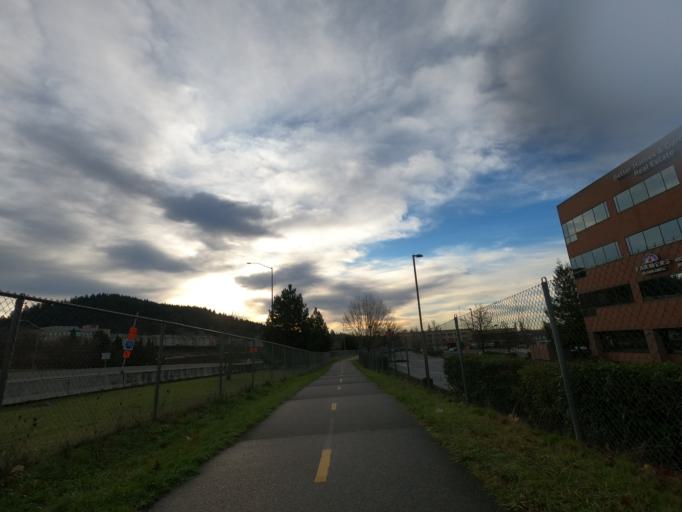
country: US
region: Oregon
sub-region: Clackamas County
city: Clackamas
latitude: 45.4326
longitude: -122.5673
